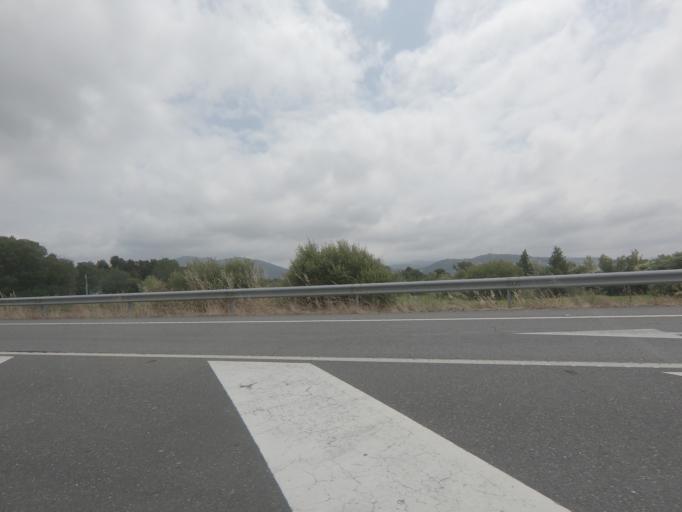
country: ES
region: Galicia
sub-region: Provincia de Pontevedra
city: O Rosal
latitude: 41.9158
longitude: -8.8214
